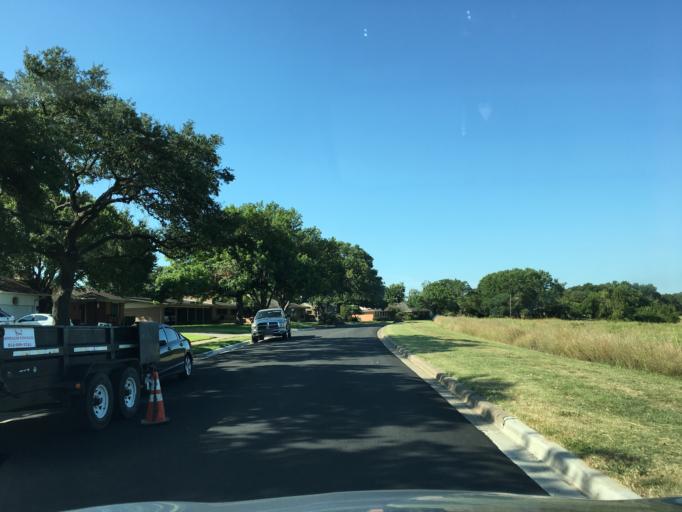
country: US
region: Texas
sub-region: Dallas County
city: Highland Park
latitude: 32.8585
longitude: -96.7102
